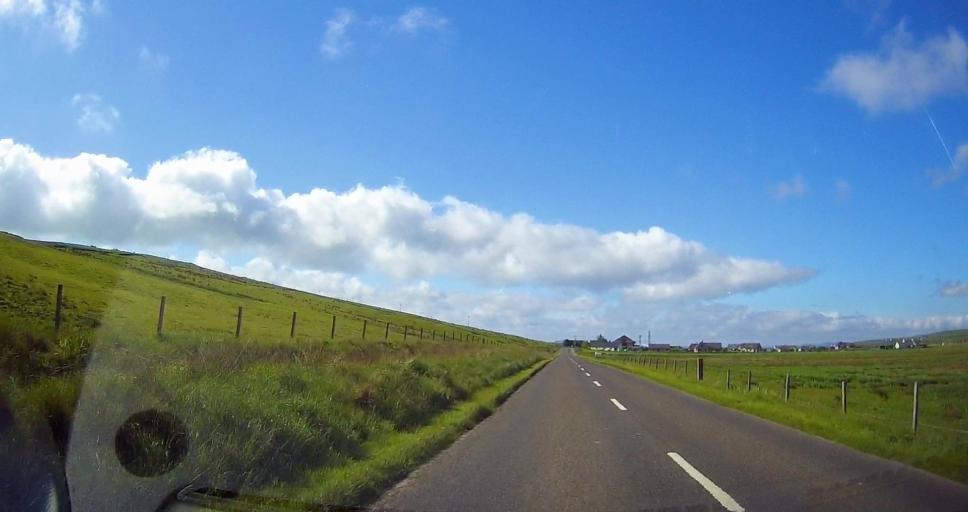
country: GB
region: Scotland
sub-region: Orkney Islands
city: Orkney
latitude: 58.9659
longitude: -2.9654
